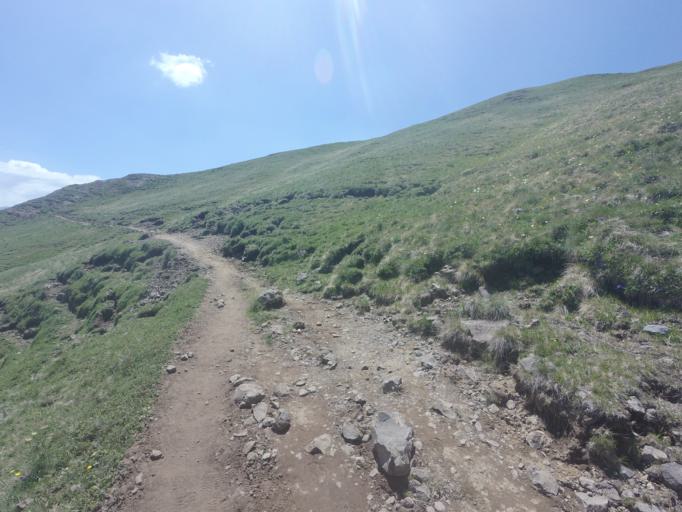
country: IT
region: Trentino-Alto Adige
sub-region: Provincia di Trento
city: Mazzin
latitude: 46.5008
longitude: 11.6870
